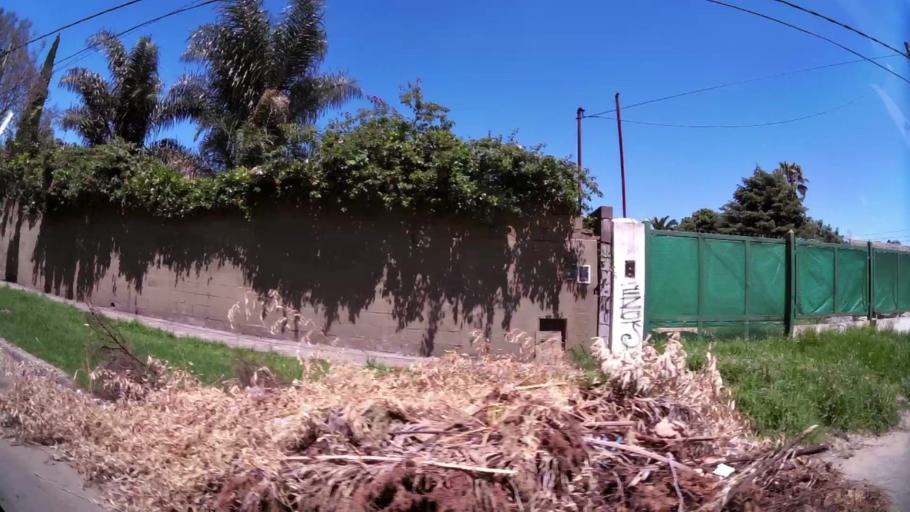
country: AR
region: Buenos Aires
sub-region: Partido de Tigre
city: Tigre
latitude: -34.4965
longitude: -58.6273
